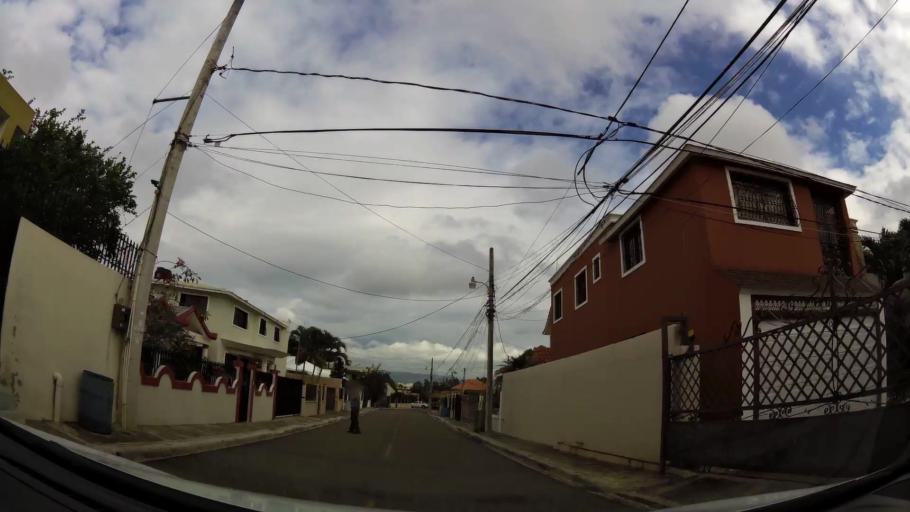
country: DO
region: Santiago
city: Santiago de los Caballeros
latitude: 19.4652
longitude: -70.6580
